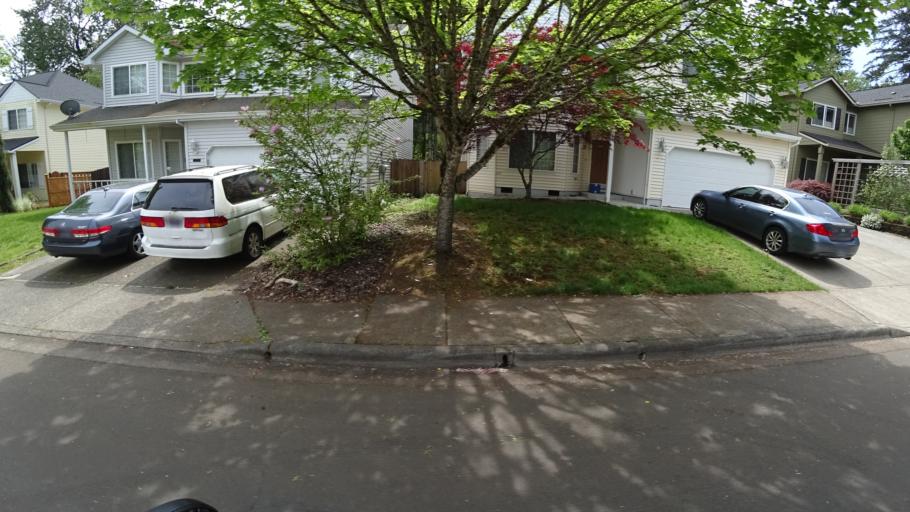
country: US
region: Oregon
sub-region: Washington County
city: Aloha
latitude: 45.4628
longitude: -122.8551
